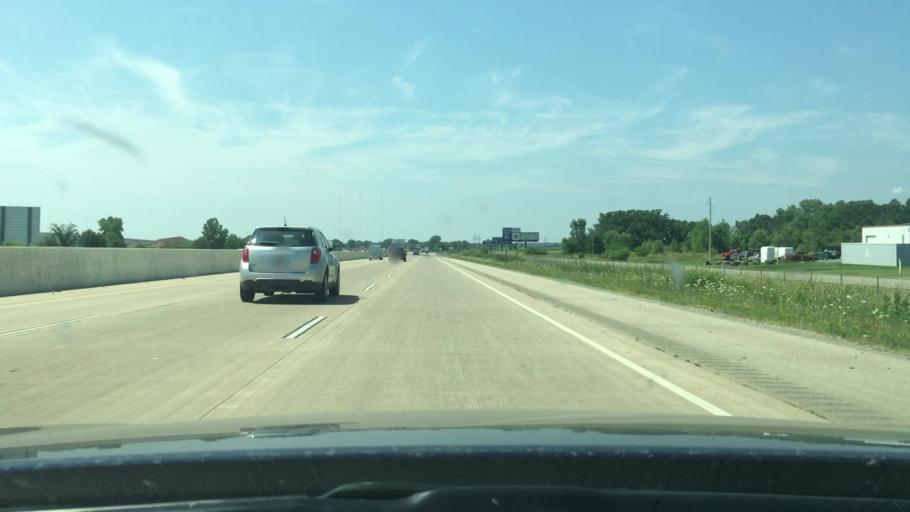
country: US
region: Wisconsin
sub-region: Winnebago County
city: Oshkosh
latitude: 44.0922
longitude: -88.5504
